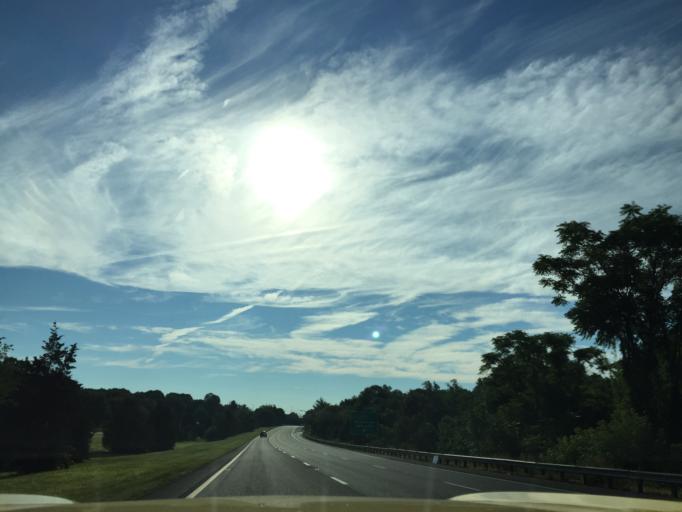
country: US
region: New Jersey
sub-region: Somerset County
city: Martinsville
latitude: 40.6463
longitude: -74.5824
